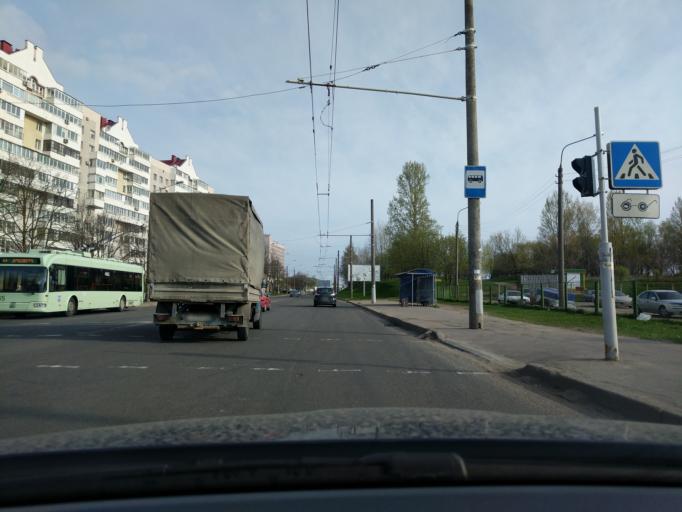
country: BY
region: Minsk
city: Novoye Medvezhino
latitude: 53.9040
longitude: 27.4630
